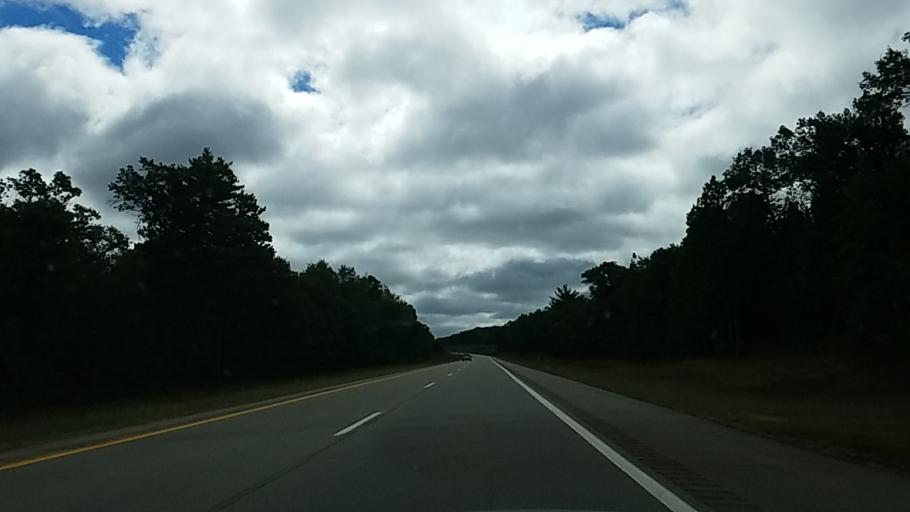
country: US
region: Michigan
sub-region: Roscommon County
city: Roscommon
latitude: 44.4992
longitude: -84.6525
